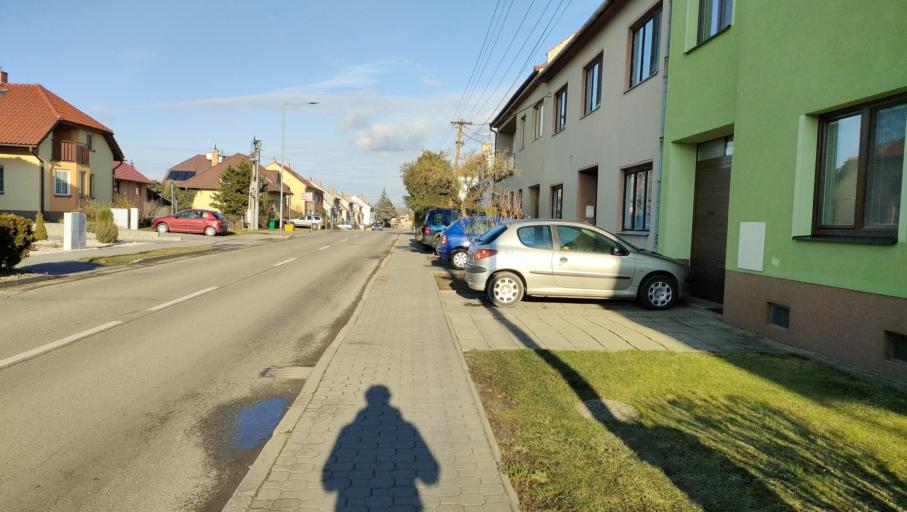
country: CZ
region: South Moravian
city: Sokolnice
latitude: 49.1334
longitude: 16.7330
